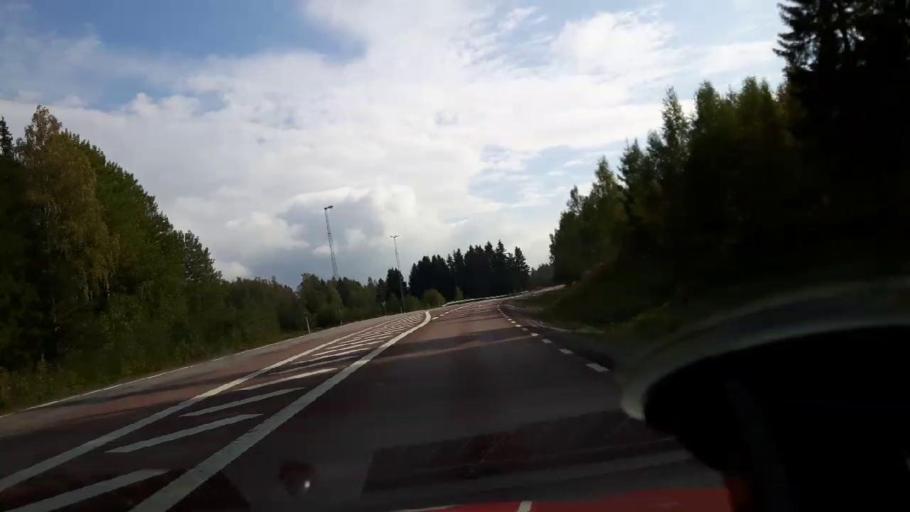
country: SE
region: Gaevleborg
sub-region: Bollnas Kommun
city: Kilafors
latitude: 61.2166
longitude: 16.7298
